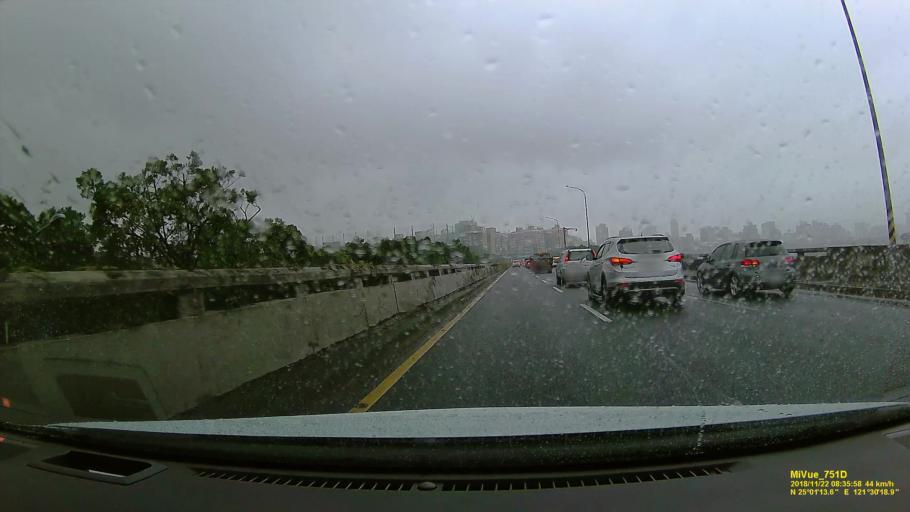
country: TW
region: Taipei
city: Taipei
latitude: 25.0205
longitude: 121.5053
